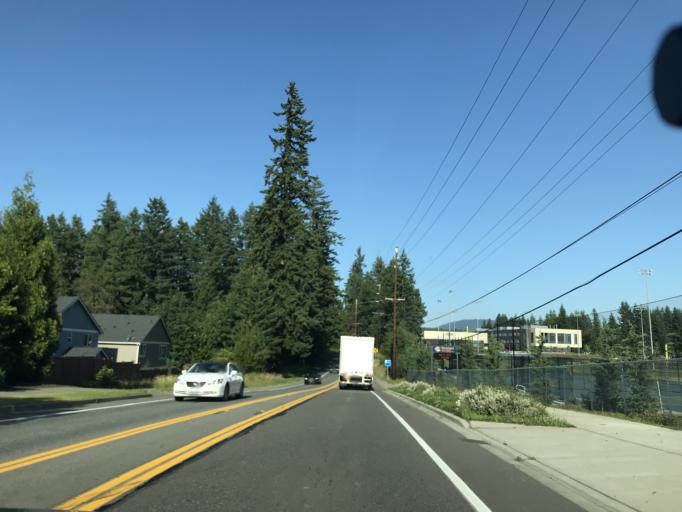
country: US
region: Washington
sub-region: King County
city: Maple Valley
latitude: 47.3580
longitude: -122.0349
